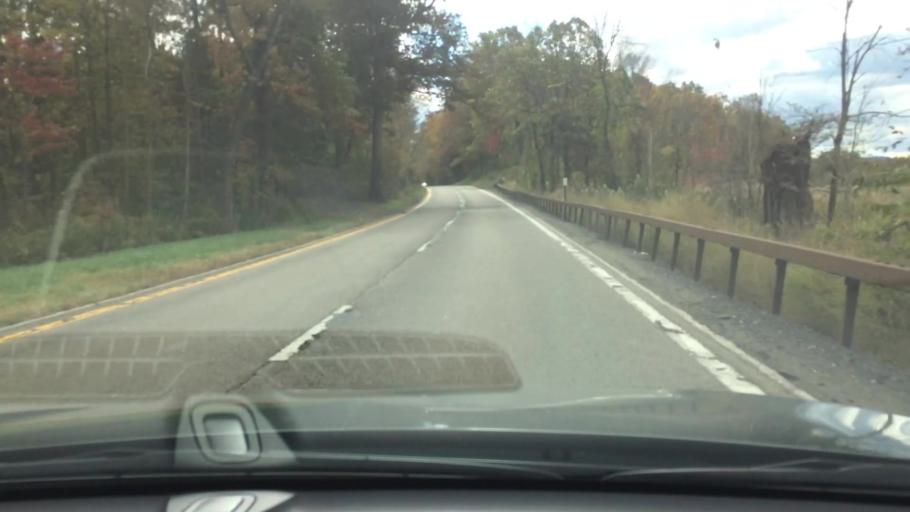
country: US
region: New York
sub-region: Dutchess County
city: Hillside Lake
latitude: 41.5637
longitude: -73.7830
